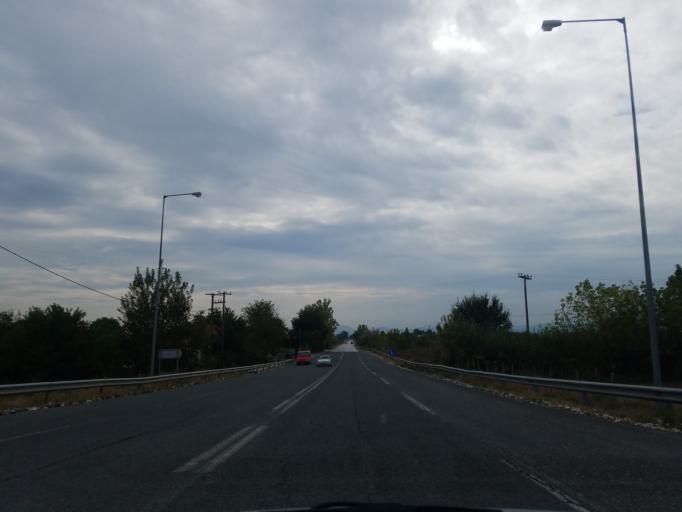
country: GR
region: Thessaly
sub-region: Nomos Kardhitsas
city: Sofades
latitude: 39.3396
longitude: 22.0828
